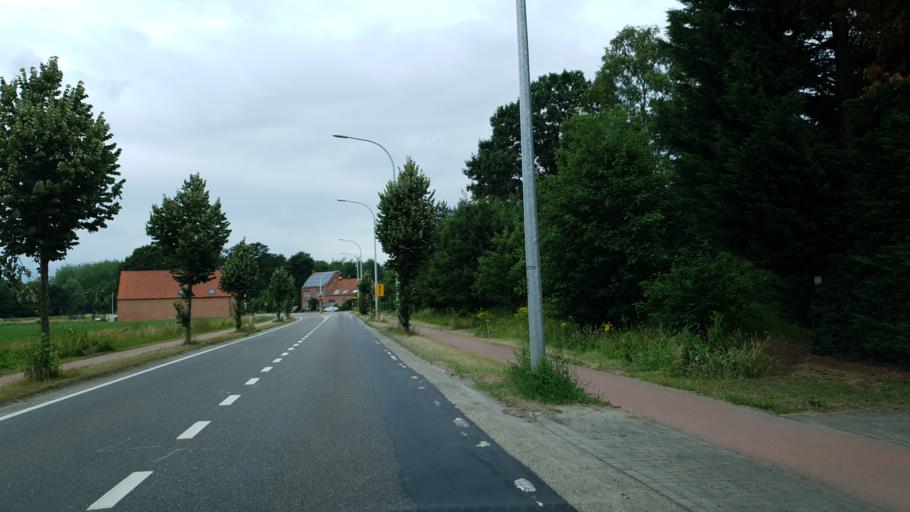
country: BE
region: Flanders
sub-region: Provincie Antwerpen
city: Geel
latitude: 51.1399
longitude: 5.0099
